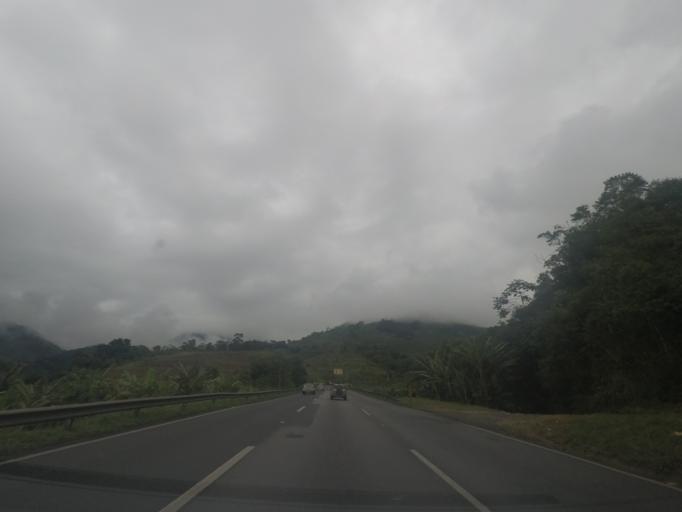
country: BR
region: Sao Paulo
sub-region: Cajati
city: Cajati
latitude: -24.8615
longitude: -48.2179
